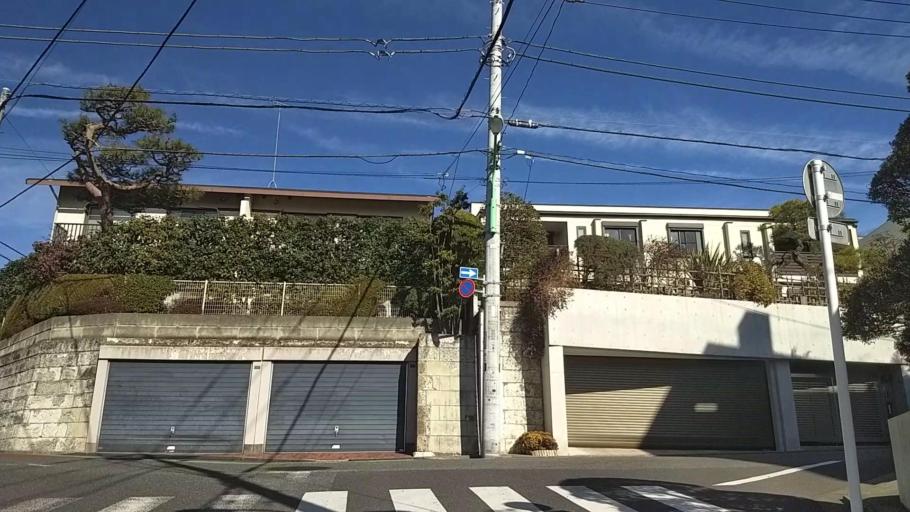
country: JP
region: Tokyo
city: Chofugaoka
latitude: 35.6202
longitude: 139.6270
